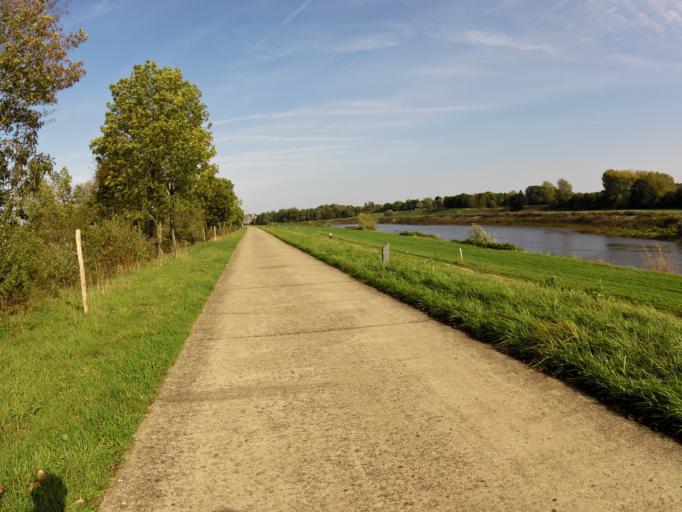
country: NL
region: Limburg
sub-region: Gemeente Stein
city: Urmond
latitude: 50.9927
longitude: 5.7571
